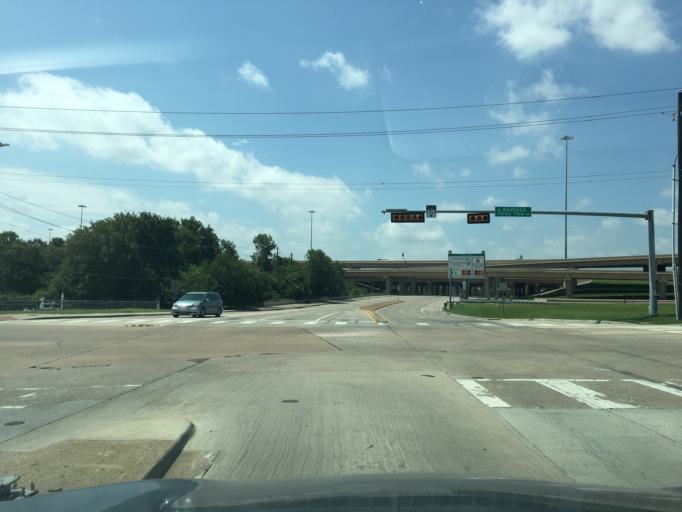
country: US
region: Texas
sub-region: Dallas County
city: Richardson
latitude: 32.9233
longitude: -96.7496
